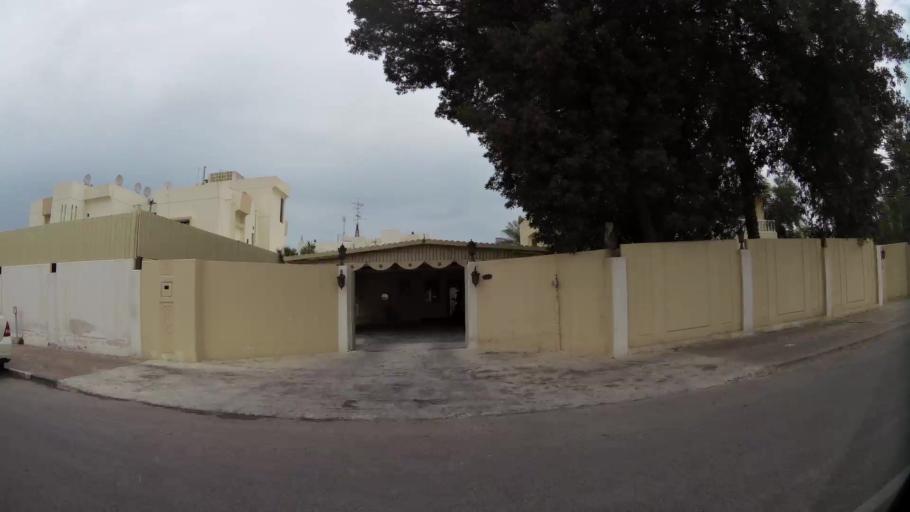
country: QA
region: Baladiyat ad Dawhah
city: Doha
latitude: 25.3327
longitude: 51.5034
